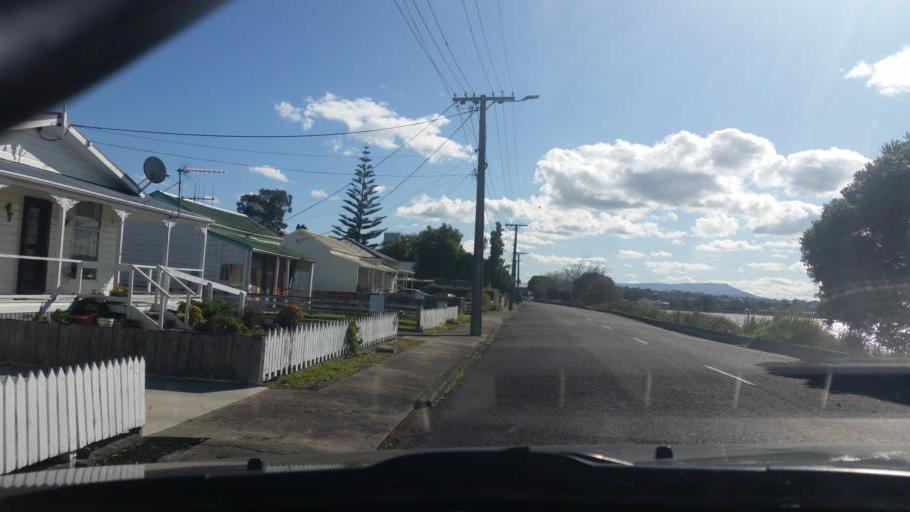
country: NZ
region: Northland
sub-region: Kaipara District
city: Dargaville
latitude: -35.9571
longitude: 173.8672
